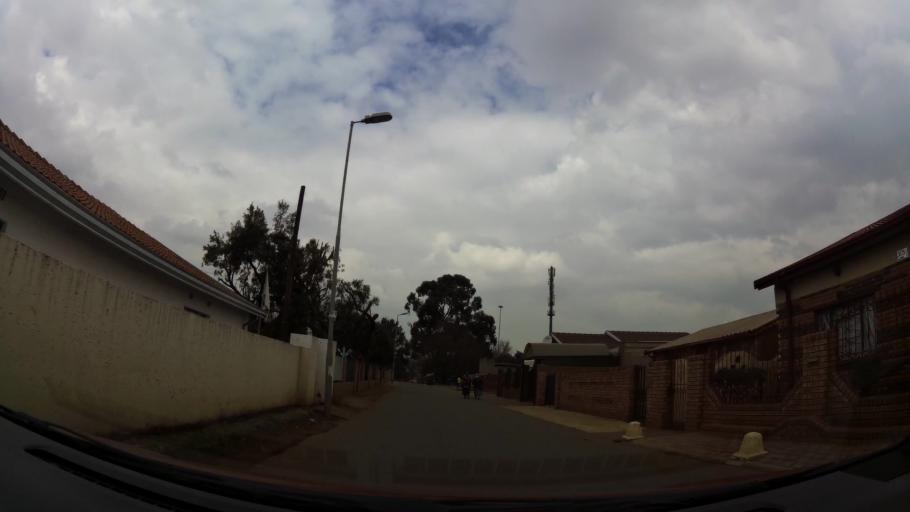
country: ZA
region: Gauteng
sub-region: City of Johannesburg Metropolitan Municipality
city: Soweto
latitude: -26.2611
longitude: 27.8356
